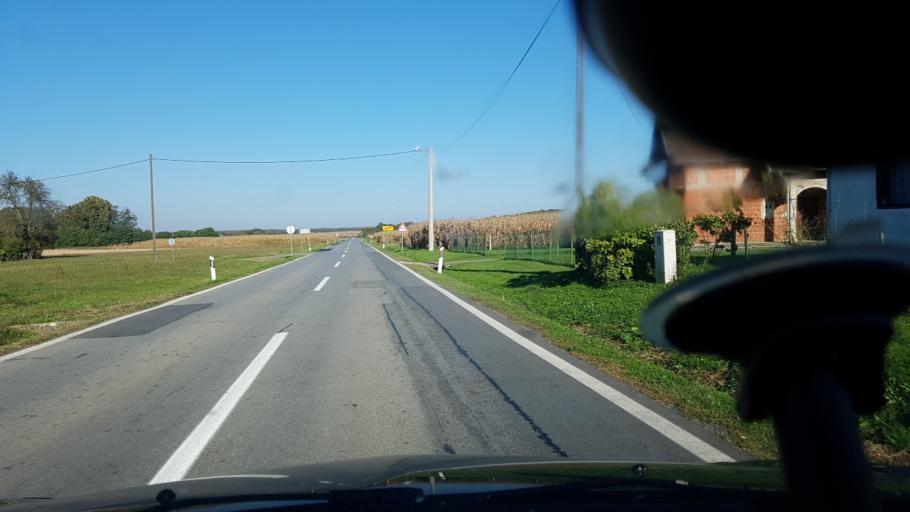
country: HR
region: Bjelovarsko-Bilogorska
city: Gudovac
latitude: 45.8243
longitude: 16.7418
